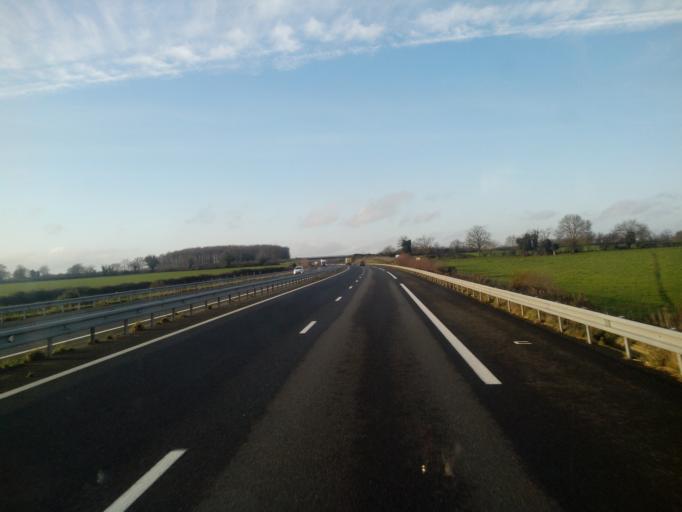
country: FR
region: Poitou-Charentes
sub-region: Departement des Deux-Sevres
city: Combrand
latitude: 46.9209
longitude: -0.6980
